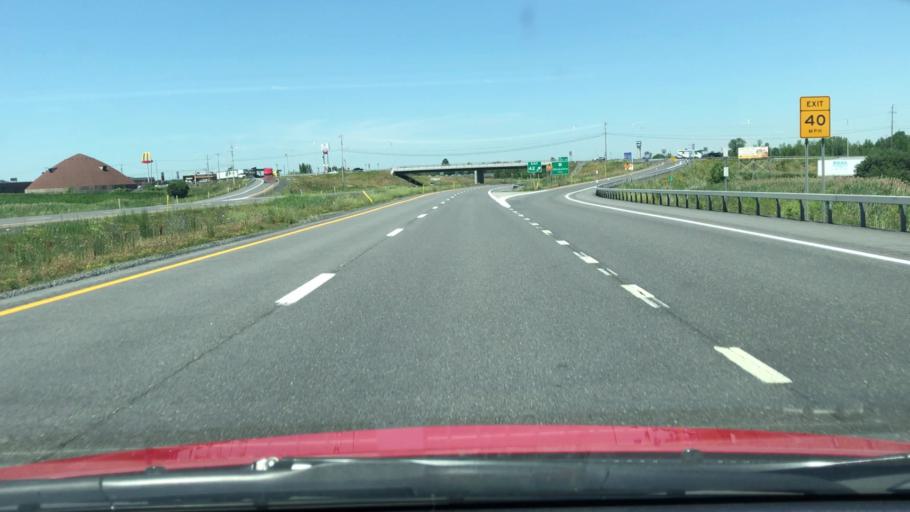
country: US
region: New York
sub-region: Clinton County
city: Champlain
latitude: 44.9783
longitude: -73.4558
